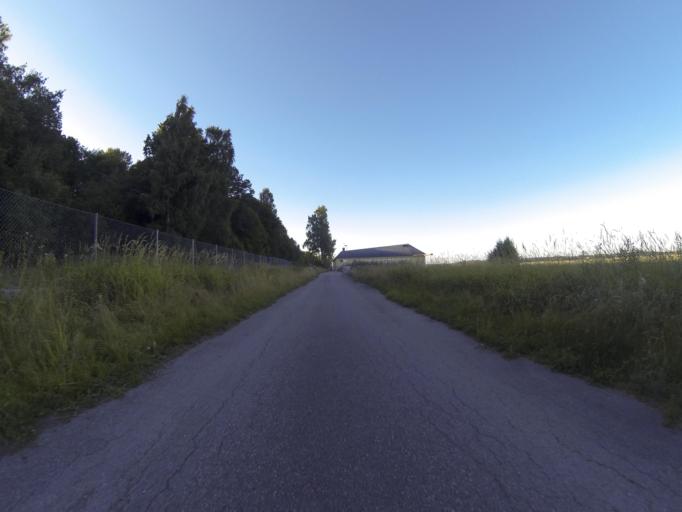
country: SE
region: Vaestmanland
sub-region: Vasteras
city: Vasteras
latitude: 59.5801
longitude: 16.6253
